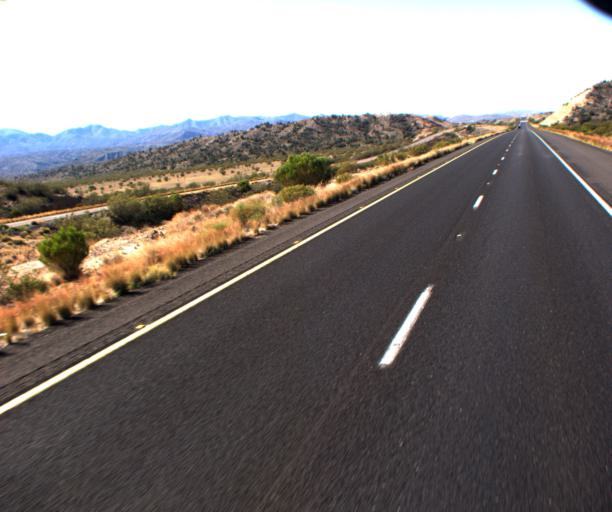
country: US
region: Arizona
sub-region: Mohave County
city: Kingman
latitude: 35.0879
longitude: -113.6662
